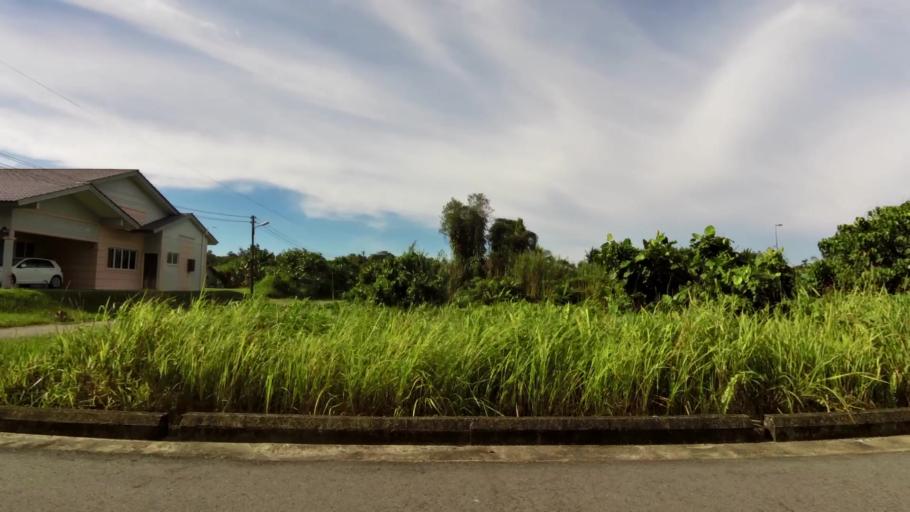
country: BN
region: Brunei and Muara
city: Bandar Seri Begawan
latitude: 4.9800
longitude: 115.0208
